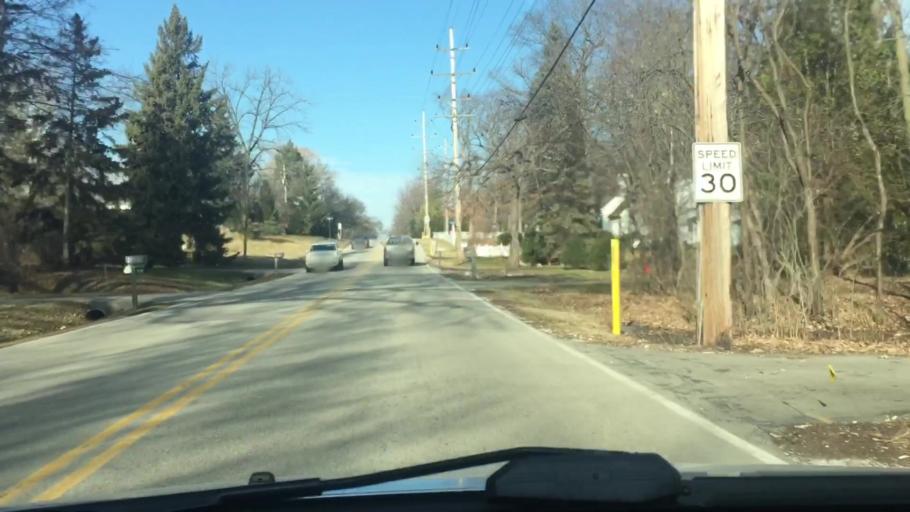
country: US
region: Wisconsin
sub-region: Waukesha County
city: Elm Grove
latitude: 43.0515
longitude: -88.0668
